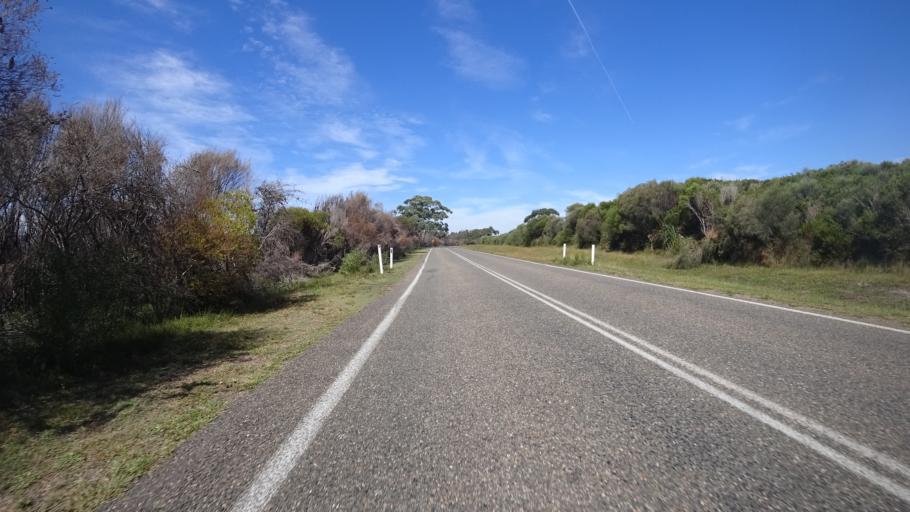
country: AU
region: New South Wales
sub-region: Shoalhaven Shire
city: Falls Creek
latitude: -35.1391
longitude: 150.7048
